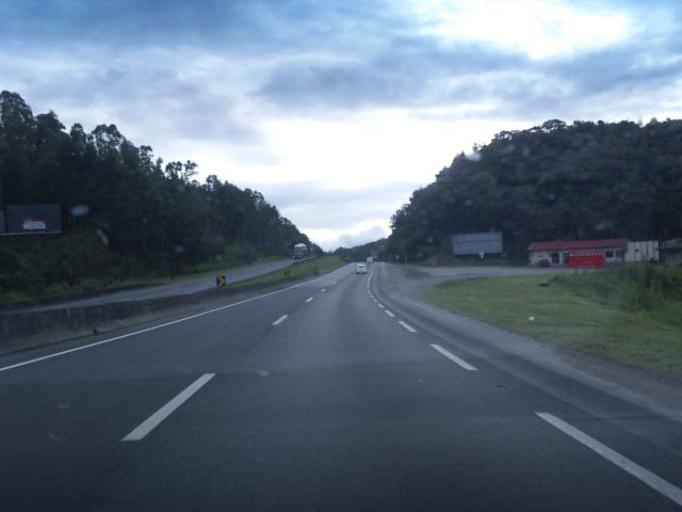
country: BR
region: Parana
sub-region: Campina Grande Do Sul
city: Campina Grande do Sul
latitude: -25.1952
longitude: -48.8902
